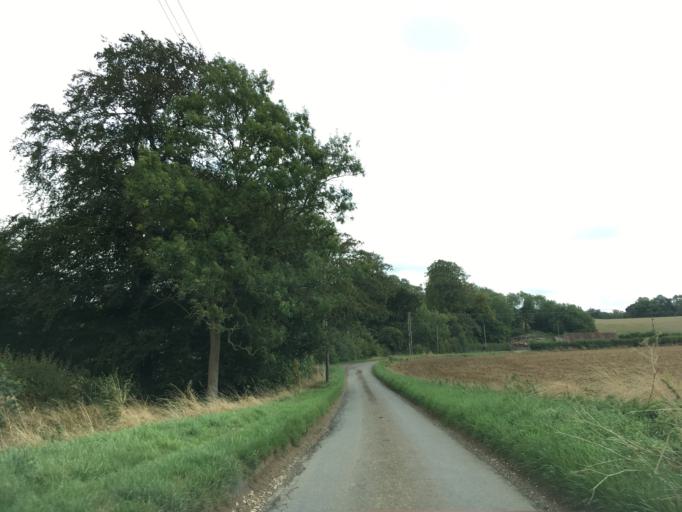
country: GB
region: England
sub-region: South Gloucestershire
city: Hinton
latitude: 51.5094
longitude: -2.3602
